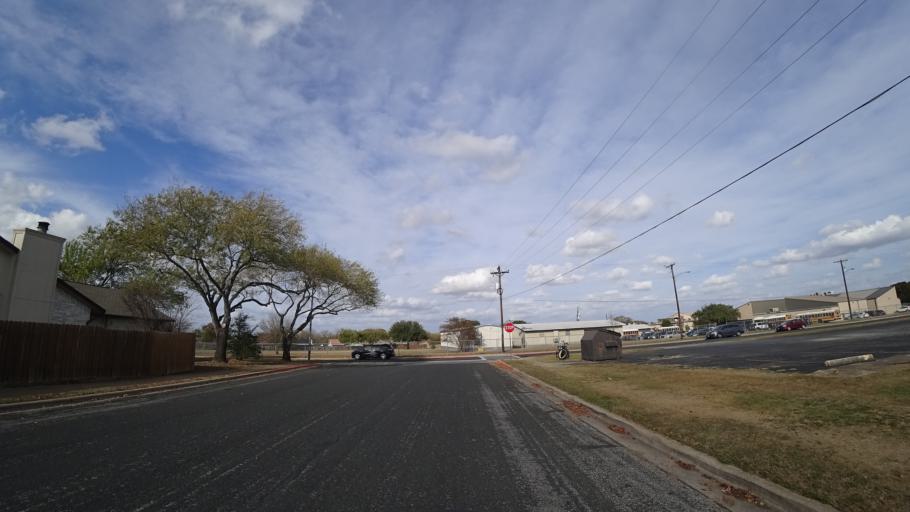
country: US
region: Texas
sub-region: Williamson County
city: Brushy Creek
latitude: 30.5107
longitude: -97.7389
